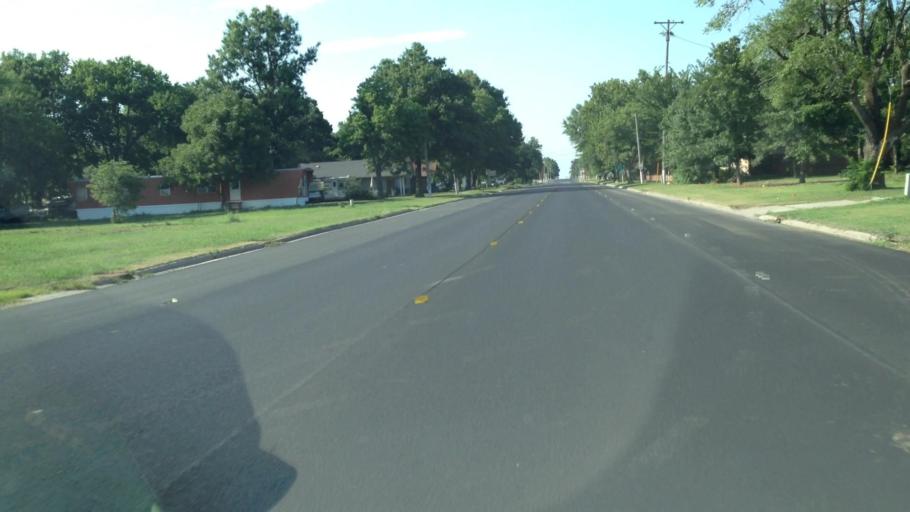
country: US
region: Kansas
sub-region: Allen County
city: Iola
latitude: 37.9098
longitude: -95.1702
